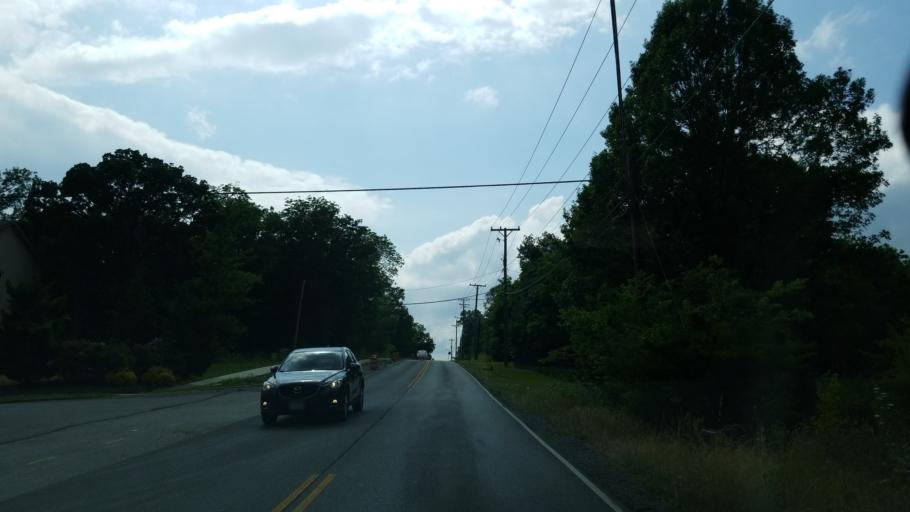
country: US
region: Tennessee
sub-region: Rutherford County
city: La Vergne
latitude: 36.0640
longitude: -86.6154
